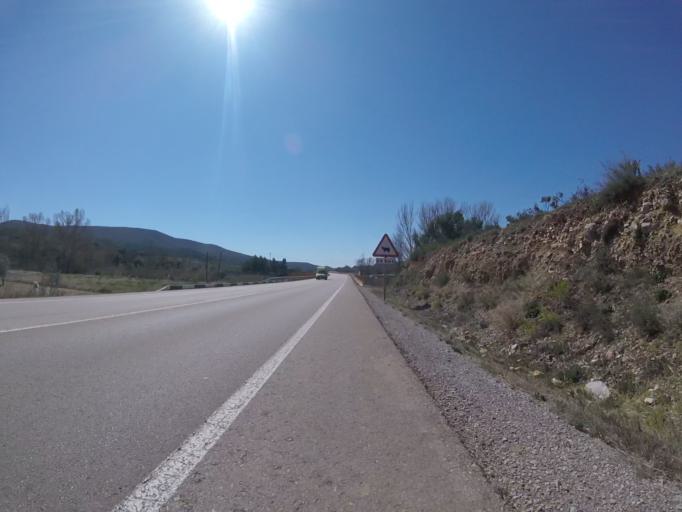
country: ES
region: Valencia
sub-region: Provincia de Castello
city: Cuevas de Vinroma
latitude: 40.3815
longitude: 0.1452
